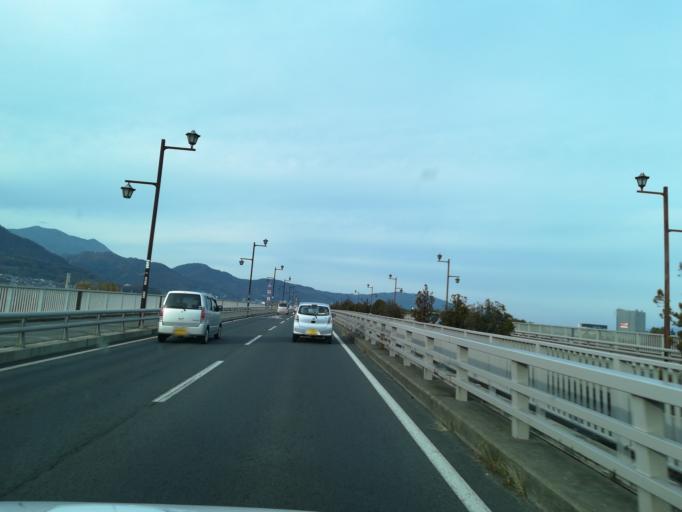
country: JP
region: Nagano
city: Nagano-shi
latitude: 36.6222
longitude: 138.1829
